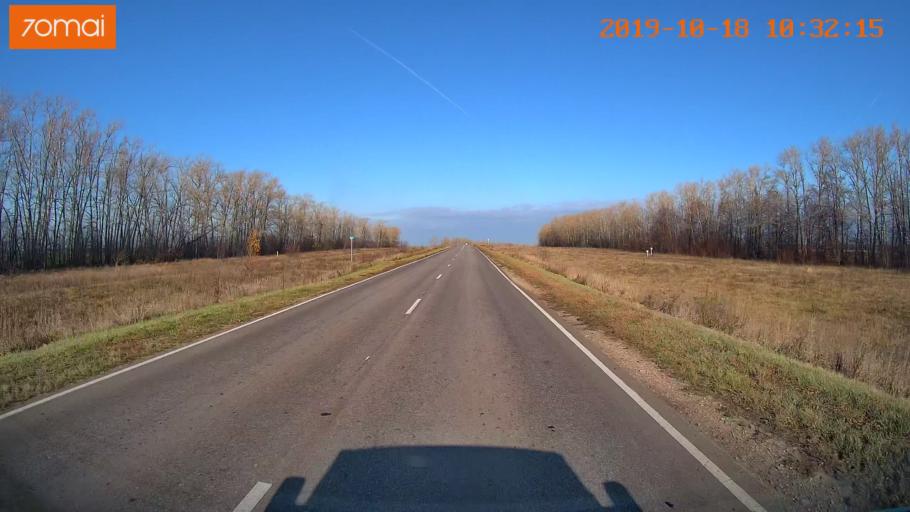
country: RU
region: Tula
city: Kurkino
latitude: 53.4914
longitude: 38.6250
